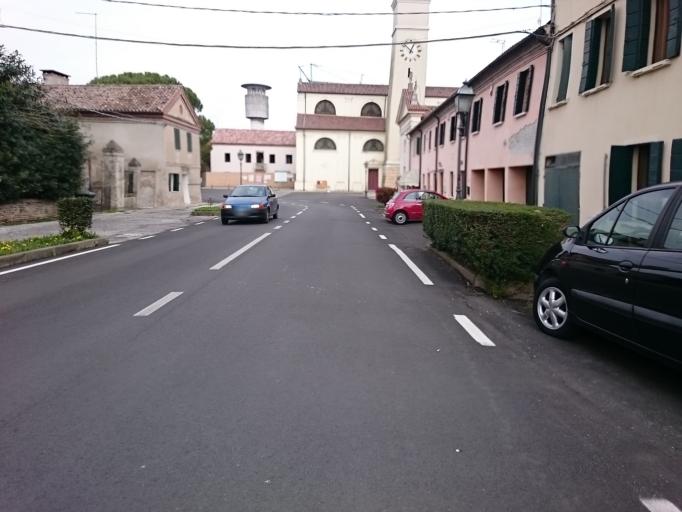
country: IT
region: Veneto
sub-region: Provincia di Padova
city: Bovolenta
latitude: 45.2693
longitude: 11.9391
